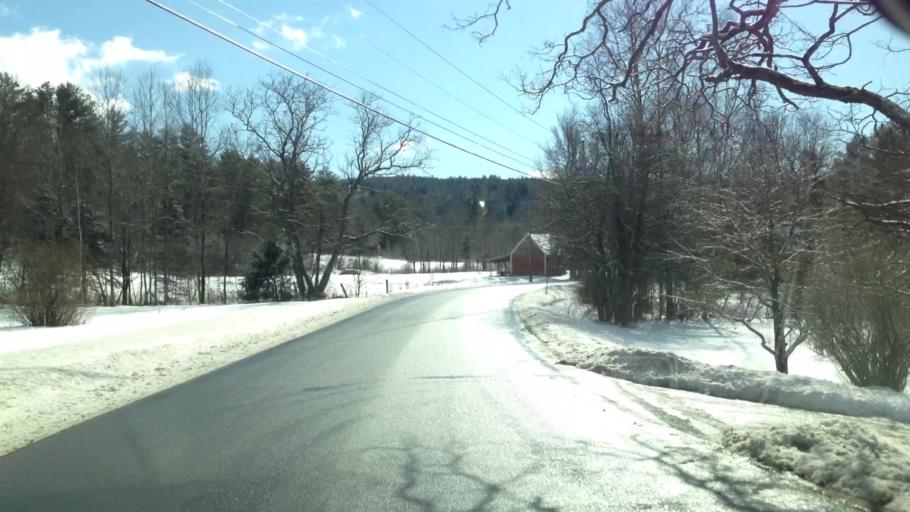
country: US
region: New Hampshire
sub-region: Grafton County
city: Haverhill
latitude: 44.0339
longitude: -72.0149
